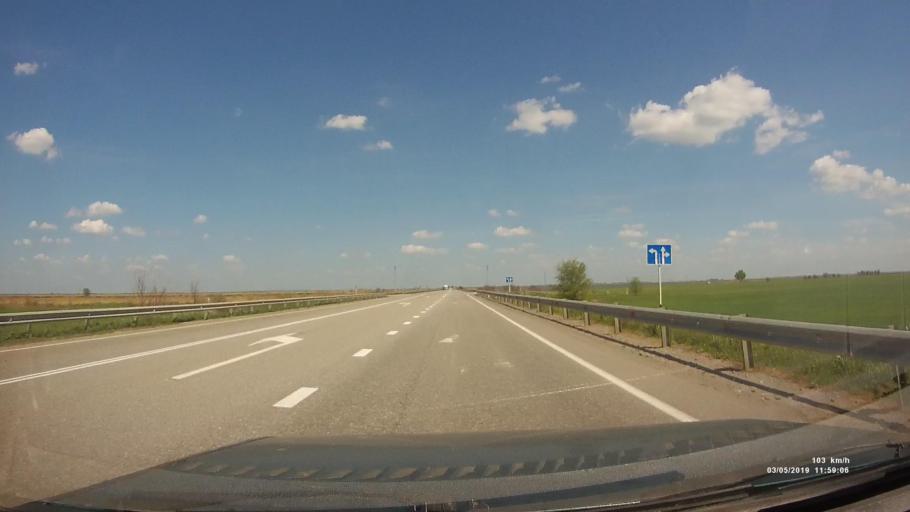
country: RU
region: Rostov
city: Bagayevskaya
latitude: 47.2302
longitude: 40.3270
